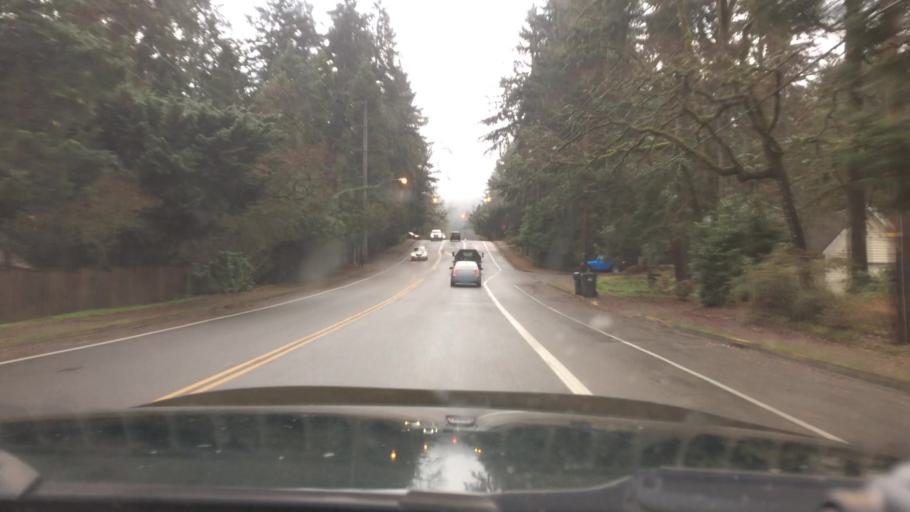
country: US
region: Oregon
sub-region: Lane County
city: Eugene
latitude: 44.0286
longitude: -123.1178
